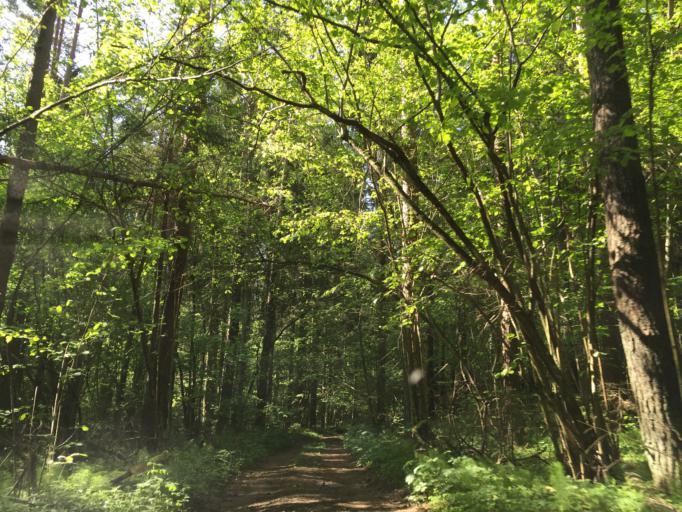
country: LV
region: Baldone
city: Baldone
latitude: 56.7977
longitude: 24.3753
